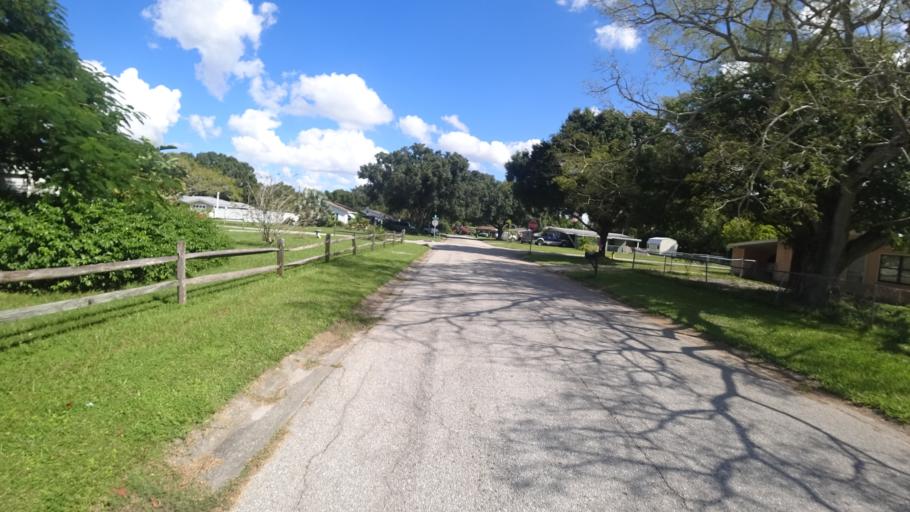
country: US
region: Florida
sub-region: Manatee County
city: South Bradenton
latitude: 27.4743
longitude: -82.5812
